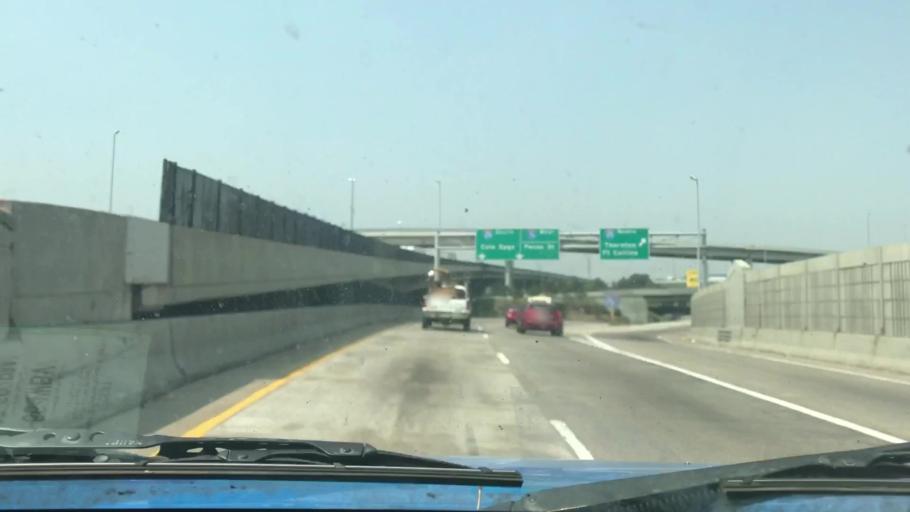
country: US
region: Colorado
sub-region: Denver County
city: Denver
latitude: 39.7800
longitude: -104.9855
